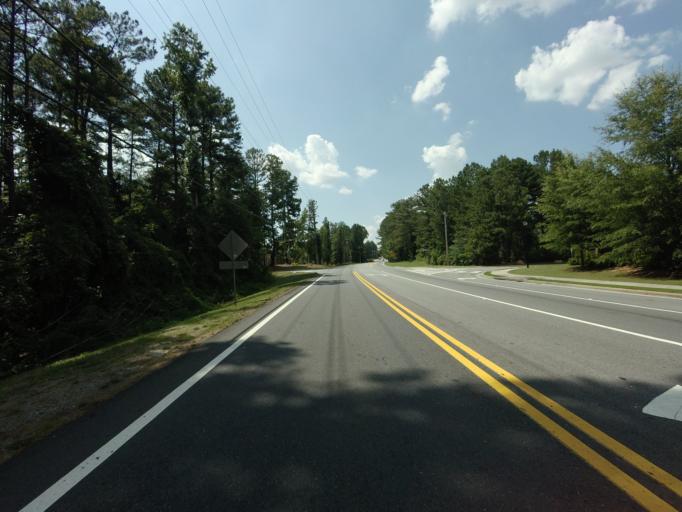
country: US
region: Georgia
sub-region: Fulton County
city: Johns Creek
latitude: 34.0583
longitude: -84.2056
